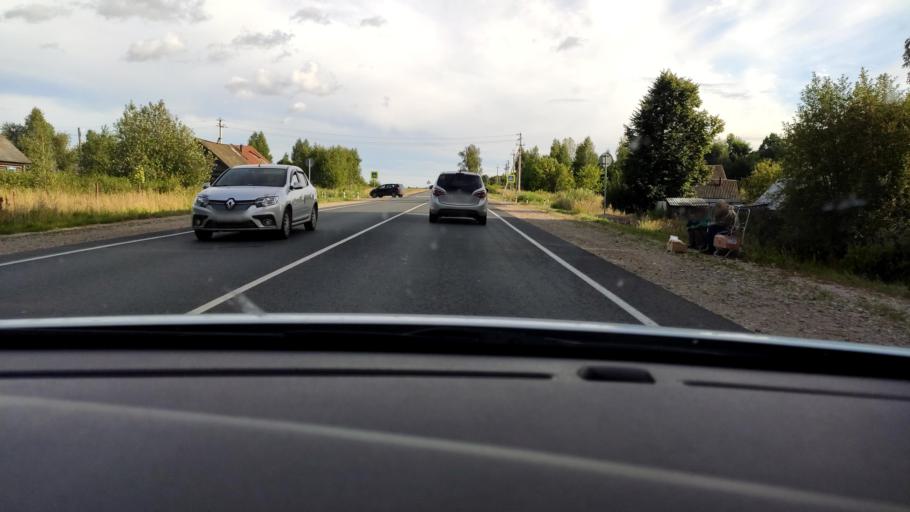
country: RU
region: Mariy-El
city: Suslonger
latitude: 56.2255
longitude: 48.2345
